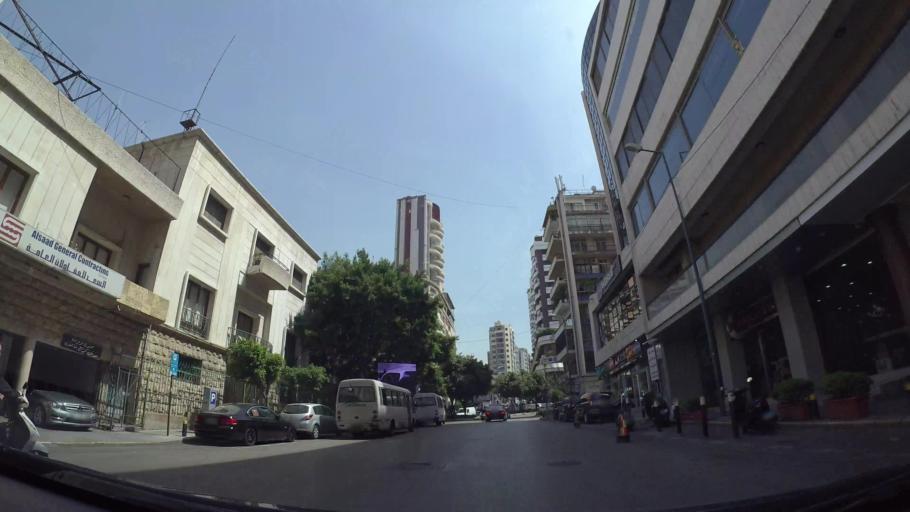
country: LB
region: Beyrouth
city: Ra's Bayrut
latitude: 33.8940
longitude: 35.4875
